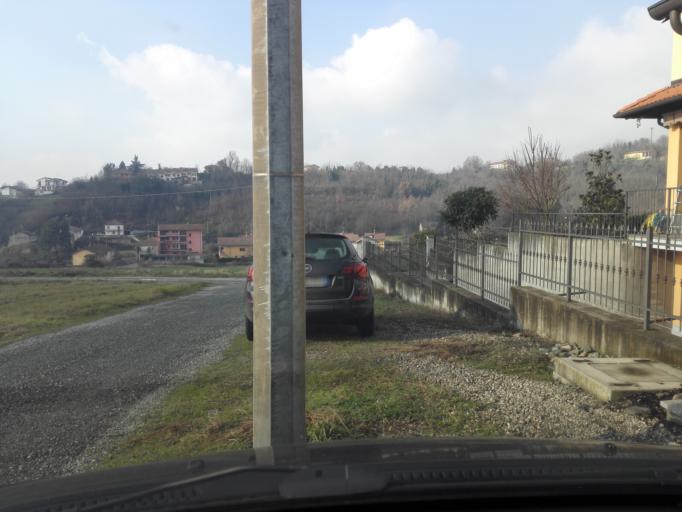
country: IT
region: Piedmont
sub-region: Provincia di Alessandria
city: Valle San Bartolomeo
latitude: 44.9597
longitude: 8.6466
